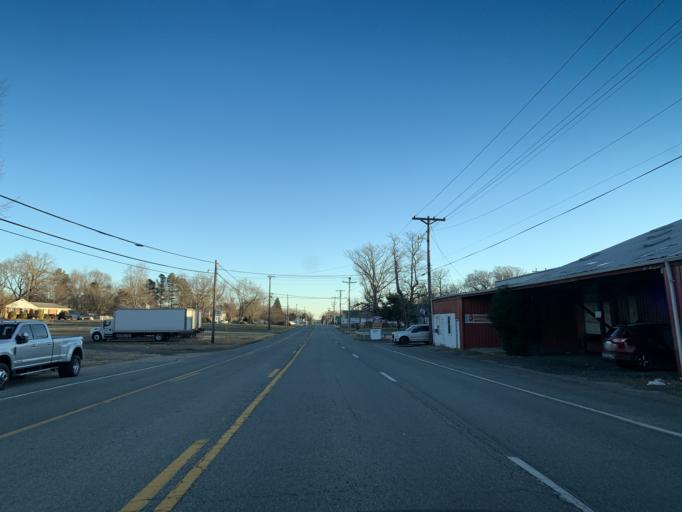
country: US
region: Maryland
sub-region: Charles County
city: Hughesville
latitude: 38.5370
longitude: -76.7863
